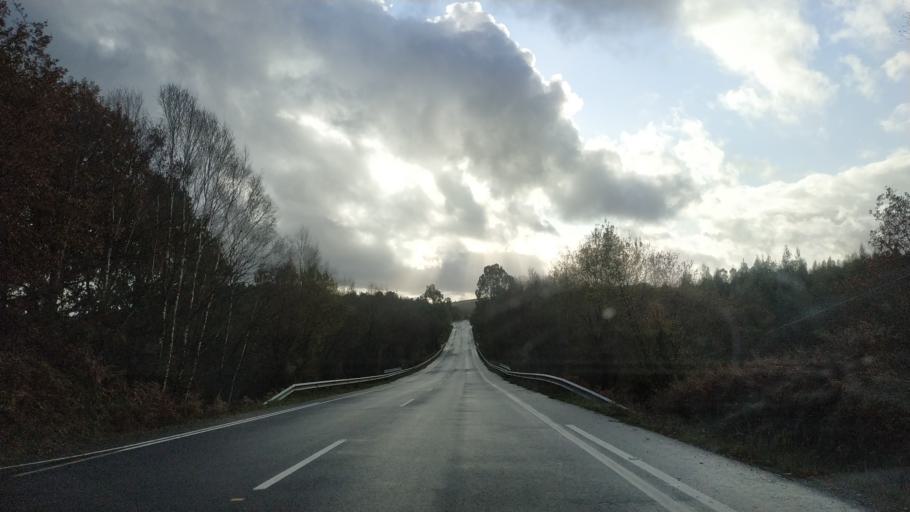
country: ES
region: Galicia
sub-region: Provincia da Coruna
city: Arzua
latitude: 42.9630
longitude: -8.1467
